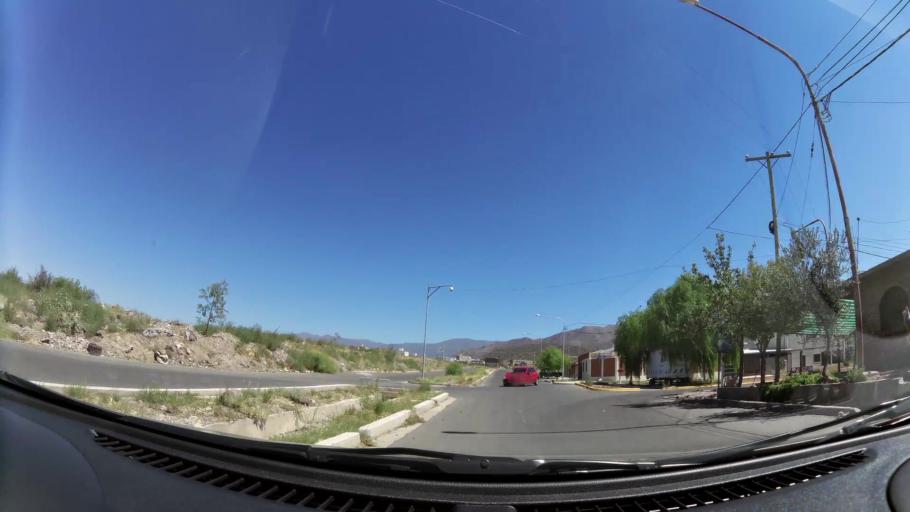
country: AR
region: Mendoza
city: Las Heras
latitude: -32.8476
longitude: -68.8724
